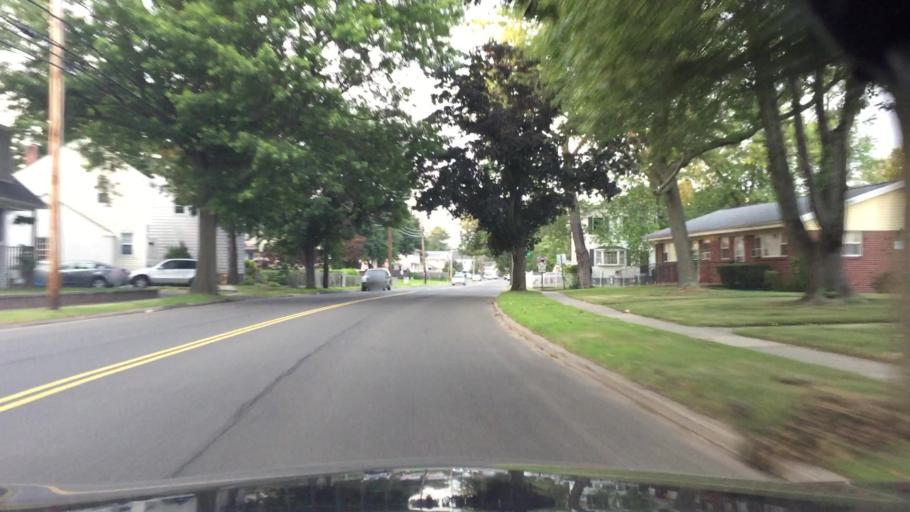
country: US
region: Connecticut
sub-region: Fairfield County
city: Stratford
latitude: 41.1765
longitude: -73.1325
